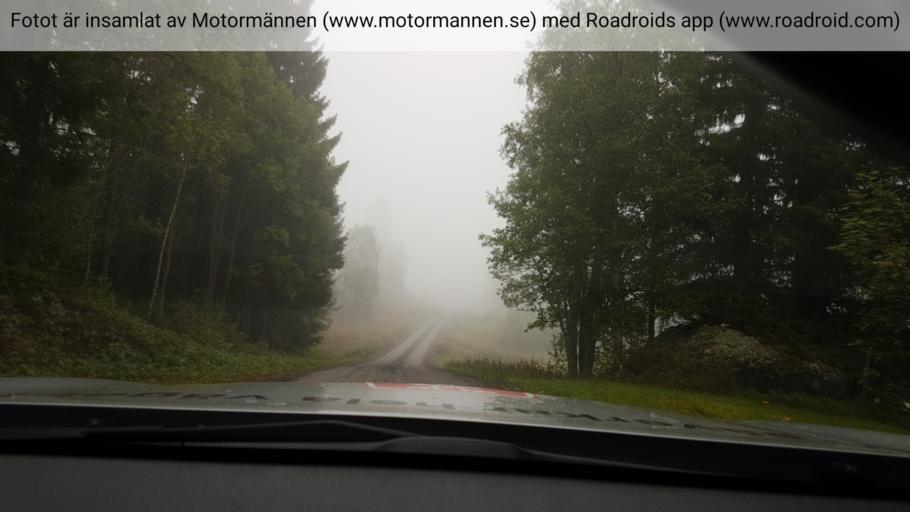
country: SE
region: Vaesterbotten
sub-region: Skelleftea Kommun
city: Burtraesk
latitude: 64.2939
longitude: 20.3973
